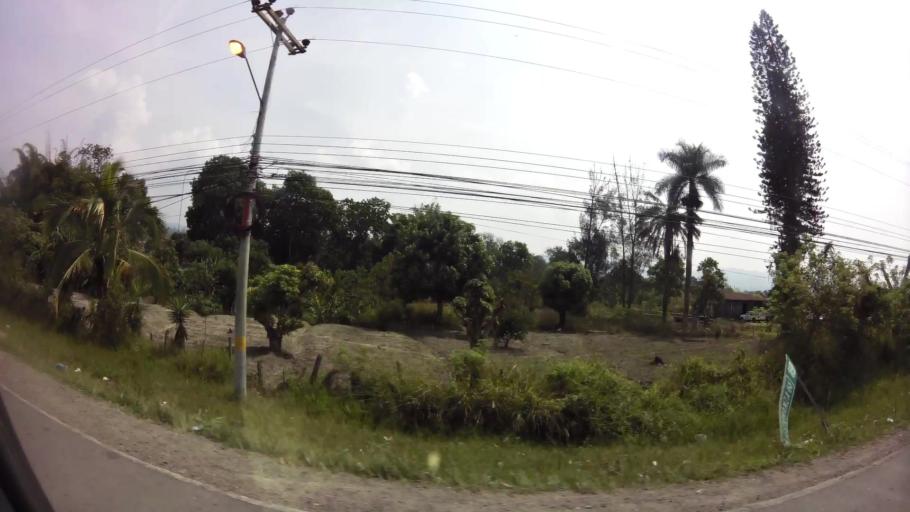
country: HN
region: Comayagua
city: El Porvenir
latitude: 14.5924
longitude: -87.8615
